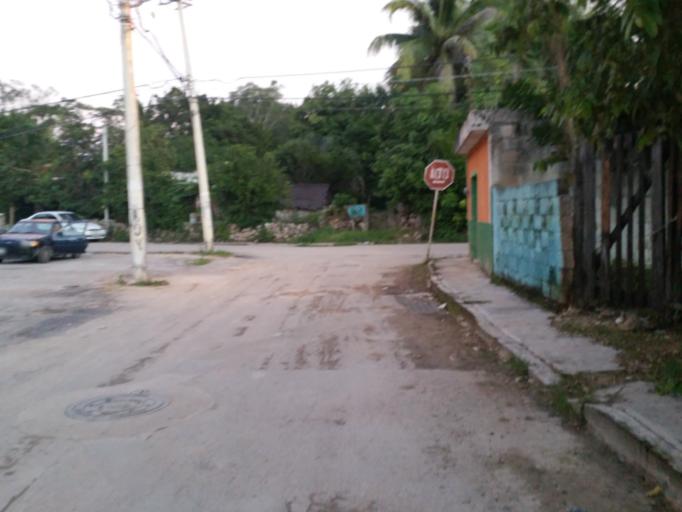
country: MX
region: Yucatan
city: Valladolid
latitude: 20.6841
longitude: -88.2103
